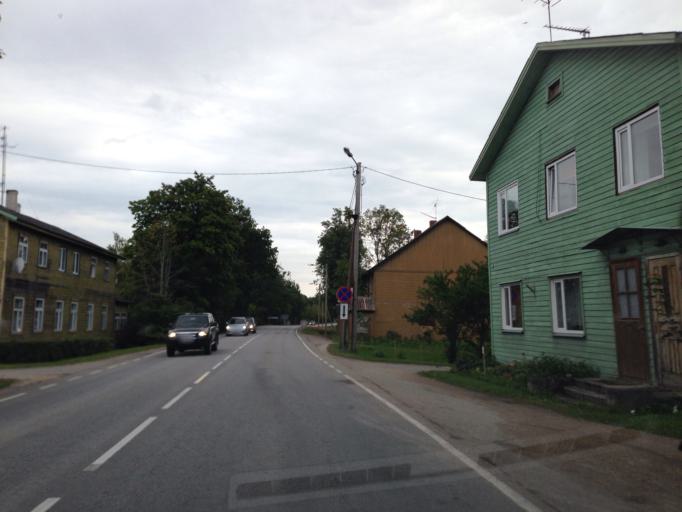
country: EE
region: Tartu
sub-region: Elva linn
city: Elva
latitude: 58.1416
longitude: 26.2473
